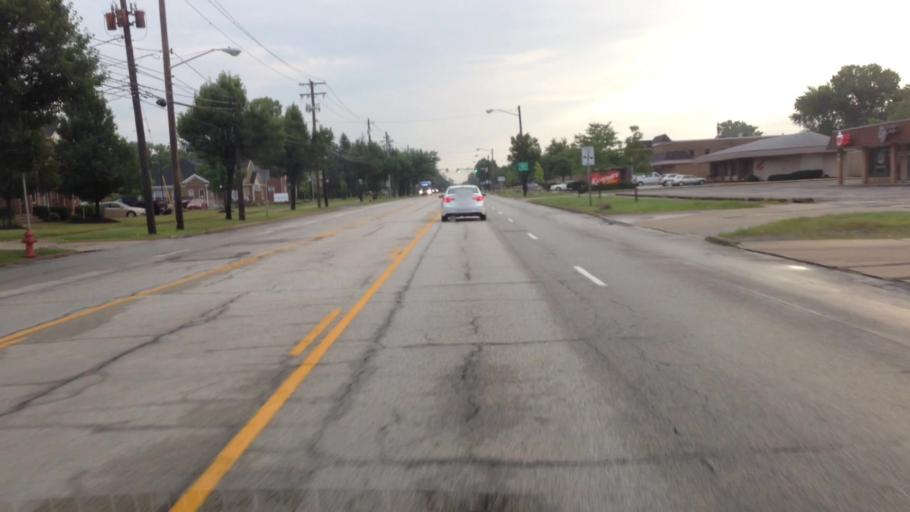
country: US
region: Ohio
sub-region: Cuyahoga County
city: Middleburg Heights
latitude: 41.3597
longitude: -81.8146
